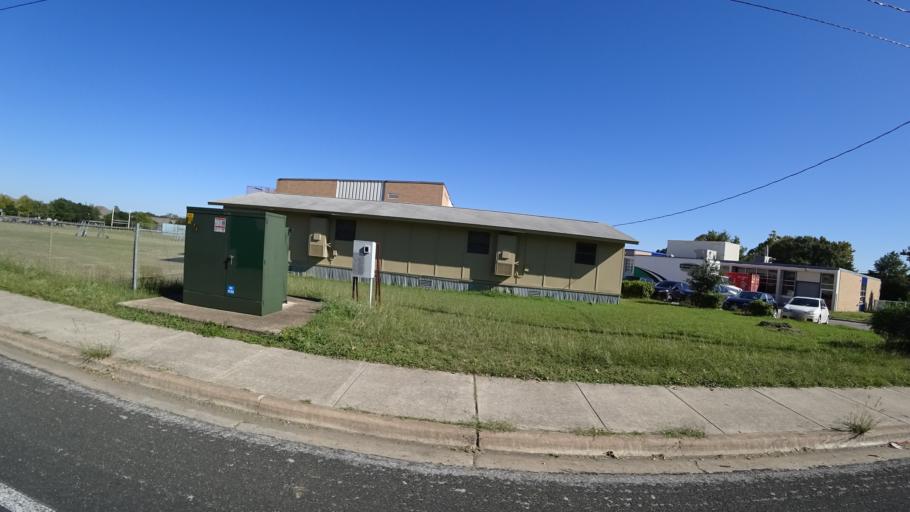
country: US
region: Texas
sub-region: Travis County
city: Rollingwood
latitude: 30.2368
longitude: -97.7893
